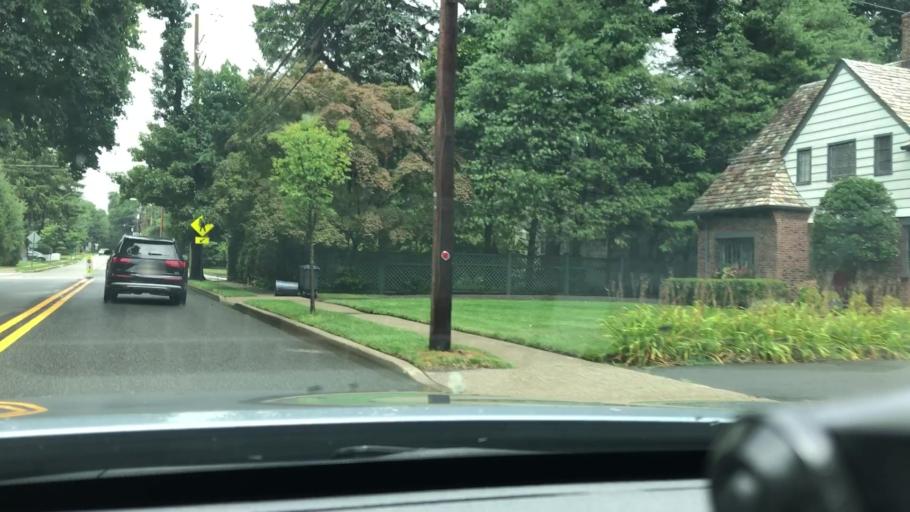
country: US
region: New Jersey
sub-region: Bergen County
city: Ho-Ho-Kus
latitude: 41.0049
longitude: -74.1075
